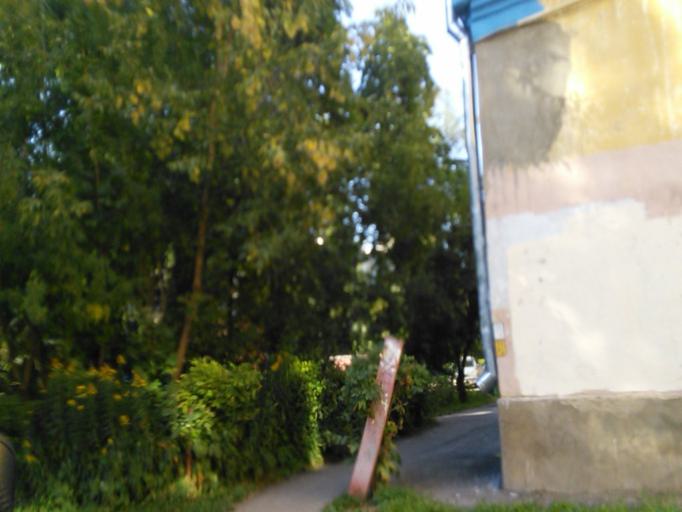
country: RU
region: Moskovskaya
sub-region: Podol'skiy Rayon
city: Podol'sk
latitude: 55.4353
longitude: 37.5638
